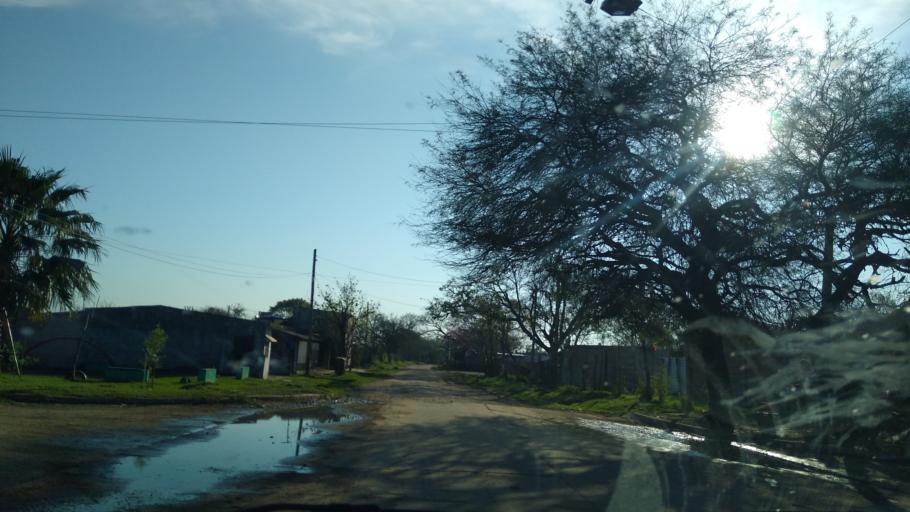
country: AR
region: Chaco
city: Barranqueras
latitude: -27.4751
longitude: -58.9562
